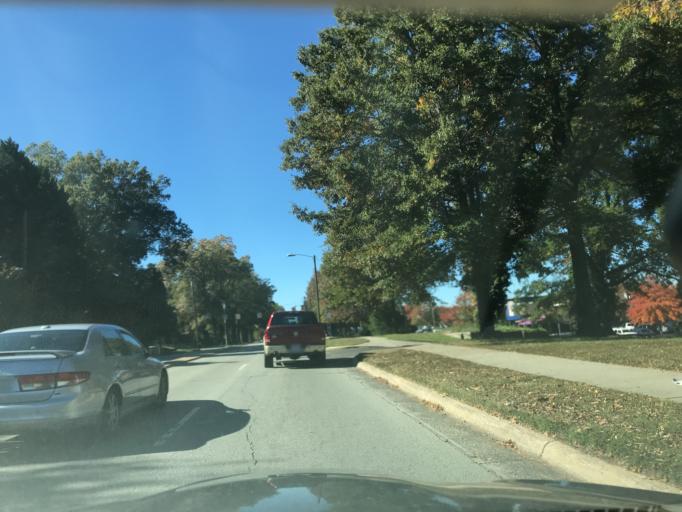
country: US
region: North Carolina
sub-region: Durham County
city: Durham
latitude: 36.0170
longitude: -78.9056
